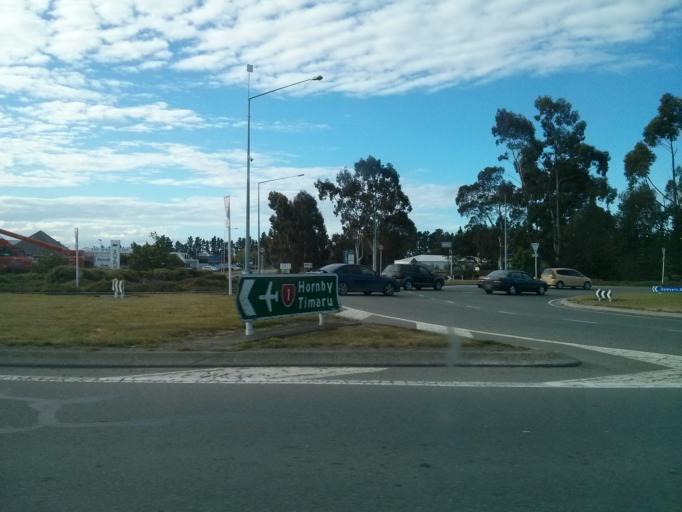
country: NZ
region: Canterbury
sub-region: Christchurch City
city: Christchurch
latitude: -43.4719
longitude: 172.5698
